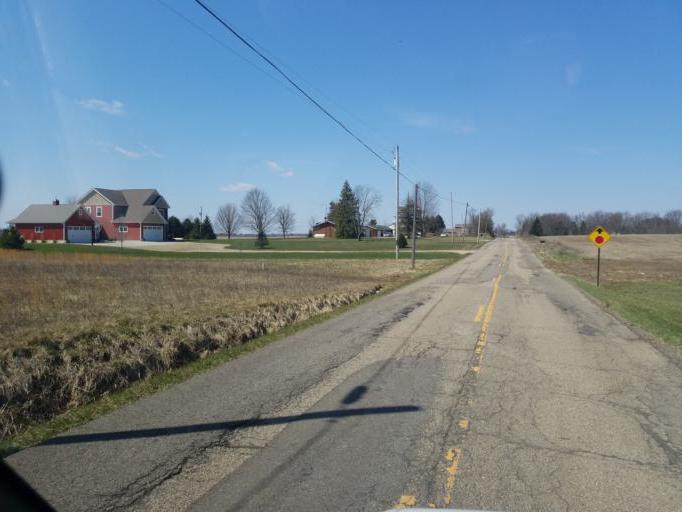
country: US
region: Ohio
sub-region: Knox County
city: Centerburg
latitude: 40.3176
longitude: -82.6581
